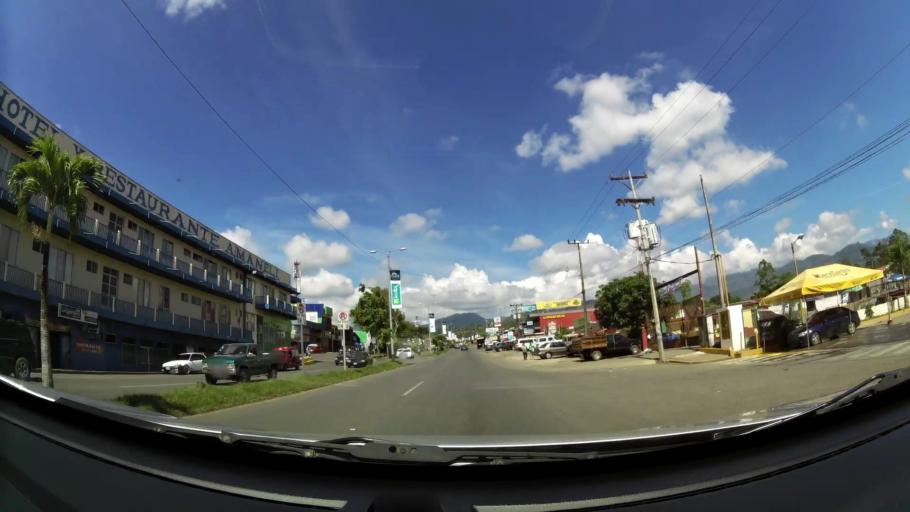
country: CR
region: San Jose
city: San Isidro
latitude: 9.3762
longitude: -83.7030
